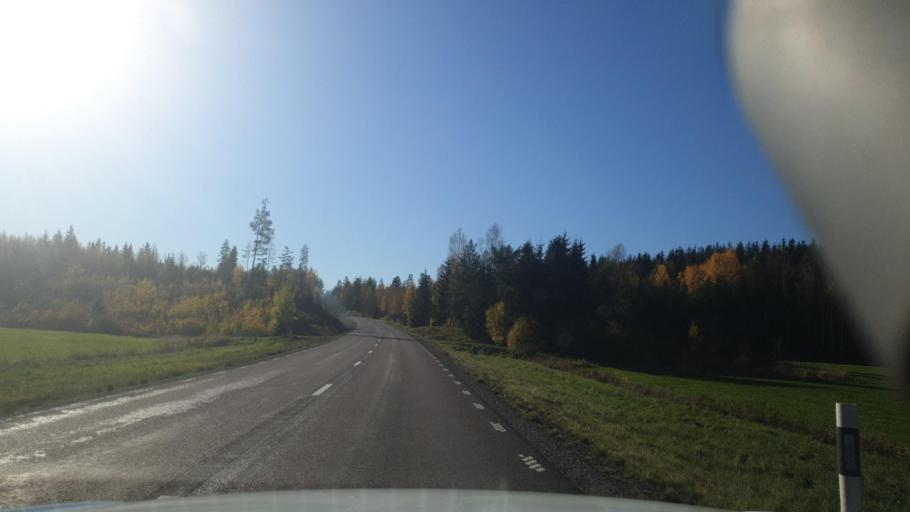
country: SE
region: Vaermland
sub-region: Arvika Kommun
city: Arvika
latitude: 59.4945
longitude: 12.7616
